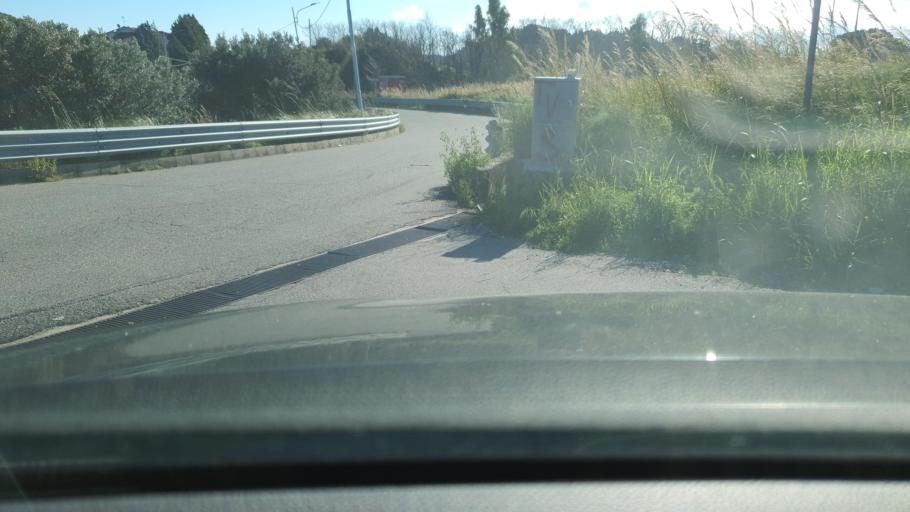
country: IT
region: Calabria
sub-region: Provincia di Catanzaro
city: Sant'Elia
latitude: 38.9500
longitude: 16.5816
